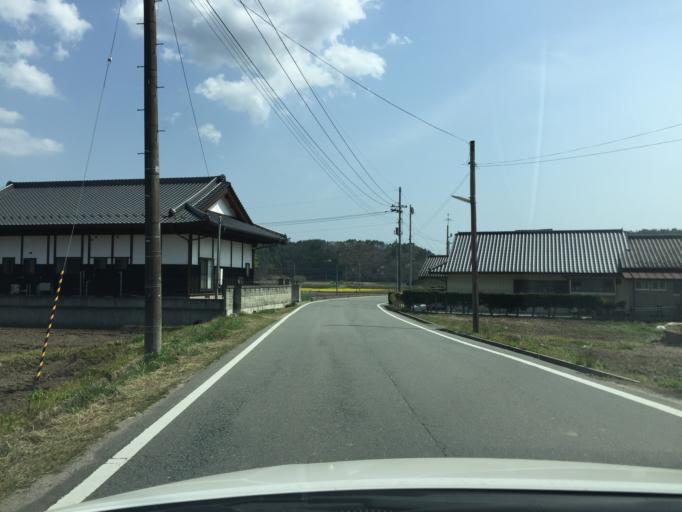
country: JP
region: Fukushima
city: Namie
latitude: 37.3159
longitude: 140.8344
